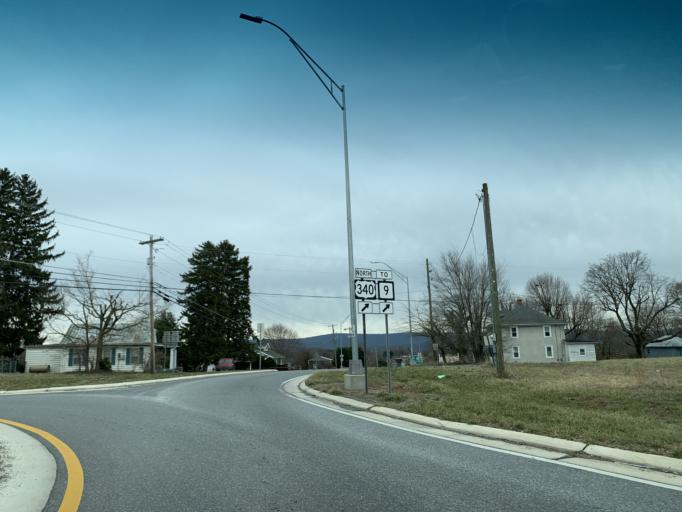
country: US
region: West Virginia
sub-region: Jefferson County
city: Charles Town
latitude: 39.2752
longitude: -77.8495
